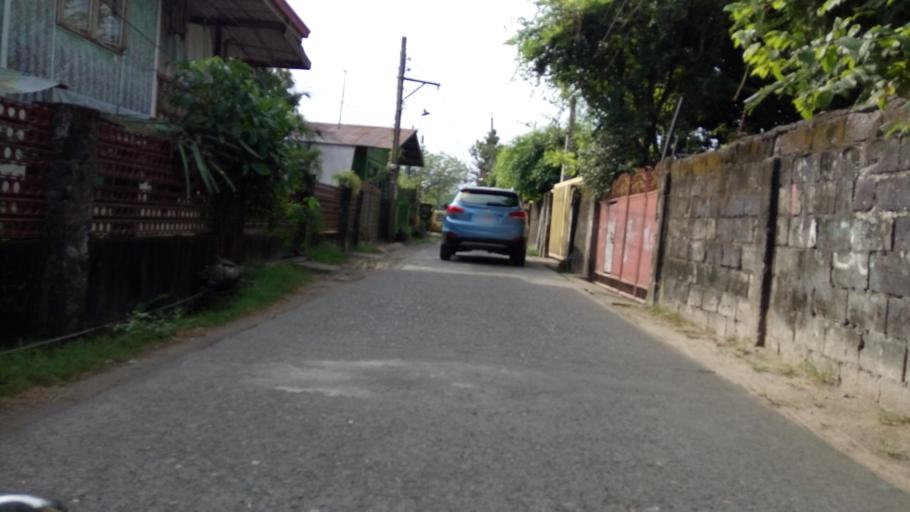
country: PH
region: Ilocos
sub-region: Province of La Union
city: Bauang
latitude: 16.5306
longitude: 120.3309
